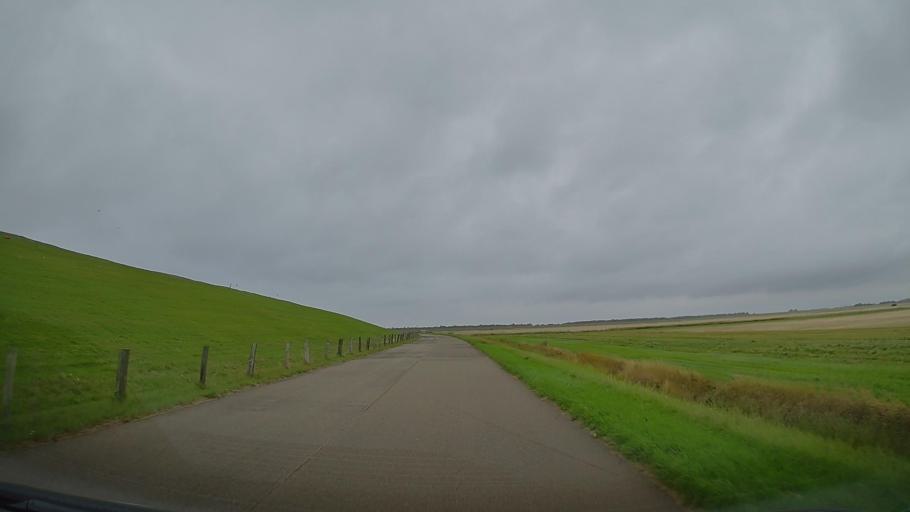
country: DE
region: Schleswig-Holstein
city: Busenwurth
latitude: 54.0610
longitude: 8.9868
